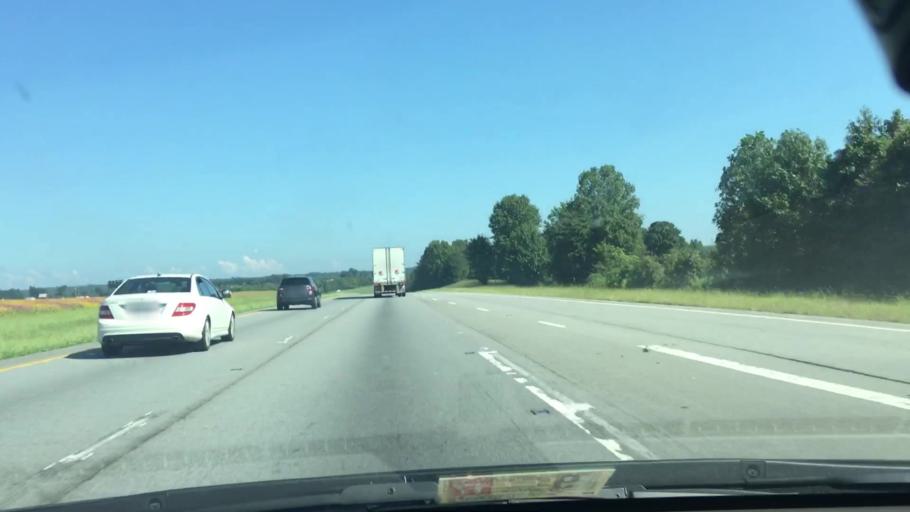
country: US
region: North Carolina
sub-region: Iredell County
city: Statesville
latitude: 35.9200
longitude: -80.8544
